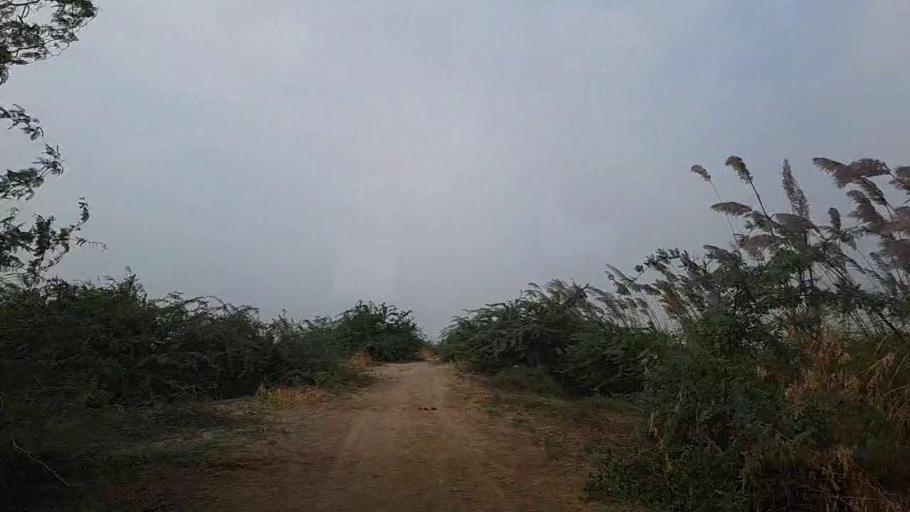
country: PK
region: Sindh
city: Mirpur Sakro
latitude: 24.6212
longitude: 67.5022
